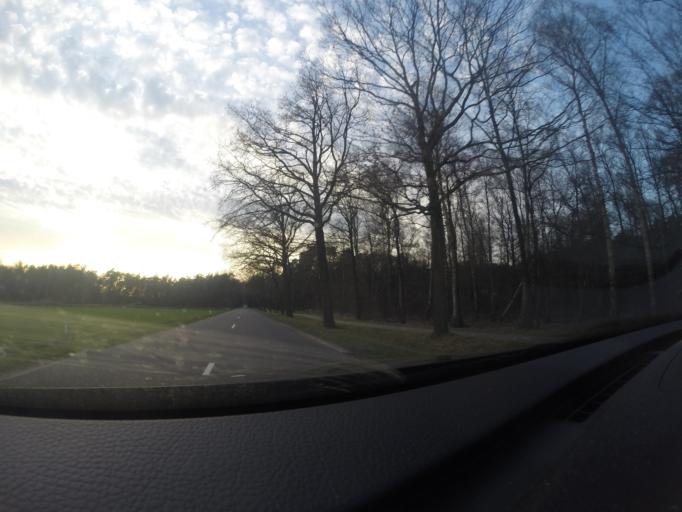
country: NL
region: Overijssel
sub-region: Gemeente Haaksbergen
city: Haaksbergen
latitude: 52.1501
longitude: 6.7874
